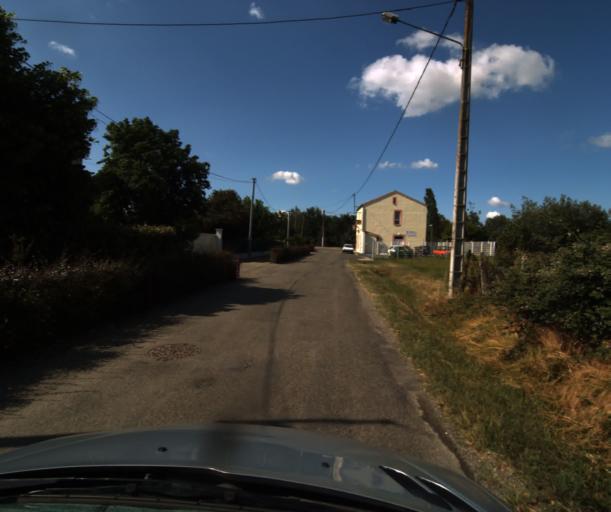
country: FR
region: Midi-Pyrenees
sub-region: Departement du Tarn-et-Garonne
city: Finhan
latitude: 43.9142
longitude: 1.2722
